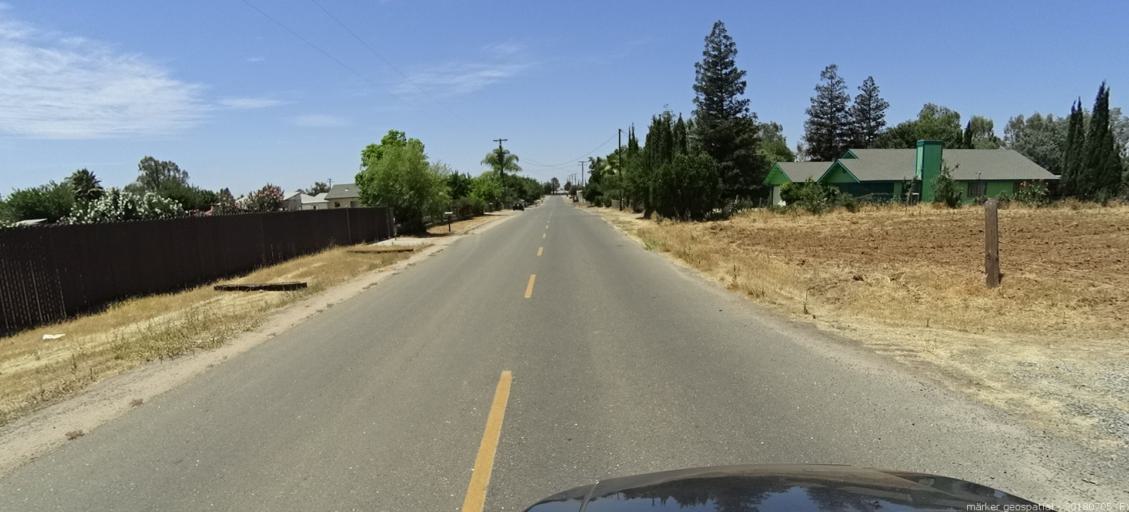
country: US
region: California
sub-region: Madera County
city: Madera
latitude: 36.9916
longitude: -120.0313
